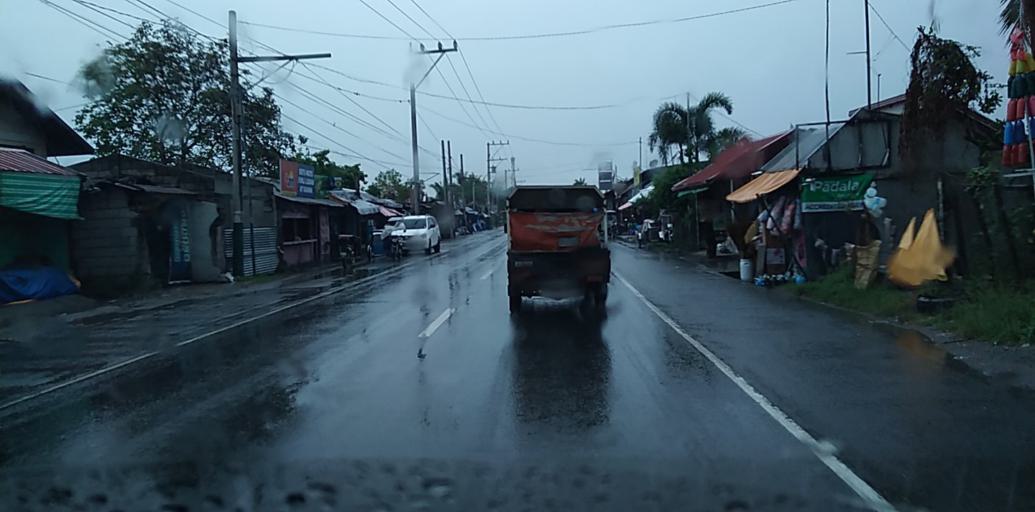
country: PH
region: Central Luzon
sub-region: Province of Bulacan
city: Bulualto
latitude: 15.2121
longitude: 120.9555
